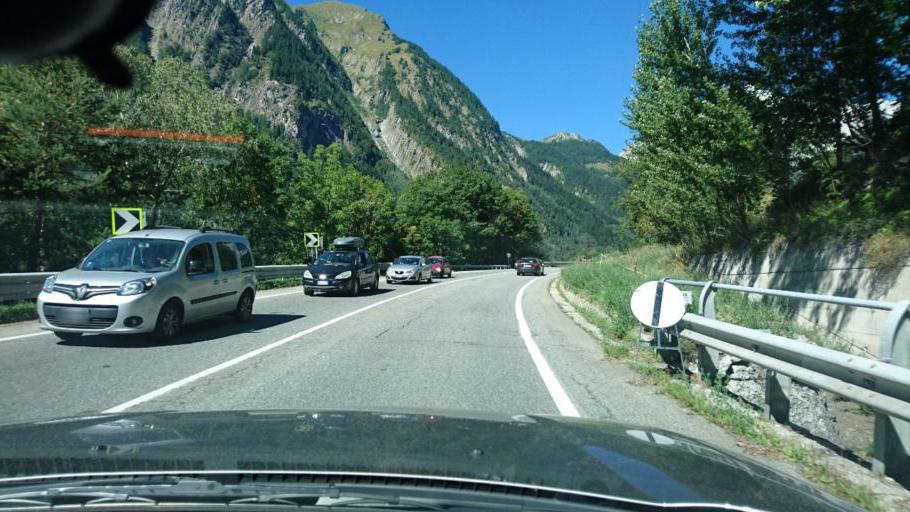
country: IT
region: Aosta Valley
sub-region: Valle d'Aosta
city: Pre Saint Didier
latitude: 45.7669
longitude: 6.9901
